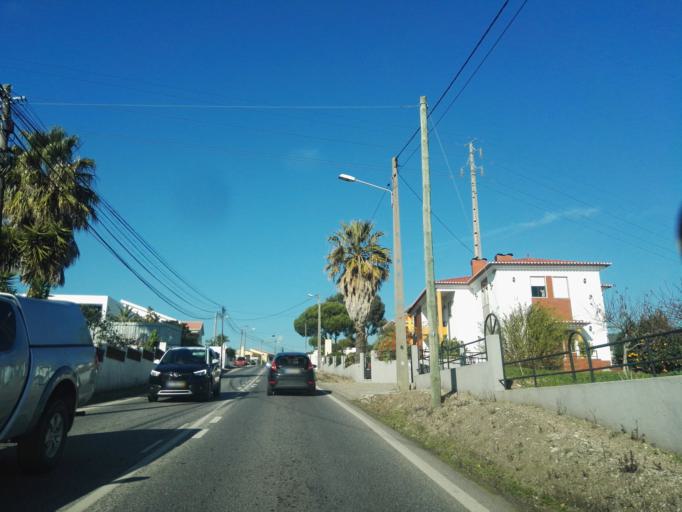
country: PT
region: Lisbon
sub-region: Loures
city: Loures
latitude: 38.8457
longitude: -9.1800
